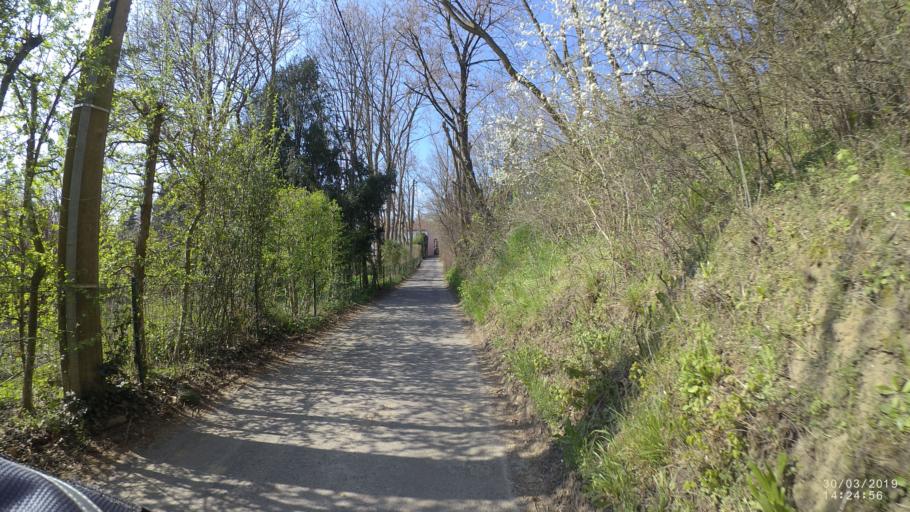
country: BE
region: Wallonia
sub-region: Province du Brabant Wallon
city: Wavre
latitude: 50.7112
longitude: 4.5776
